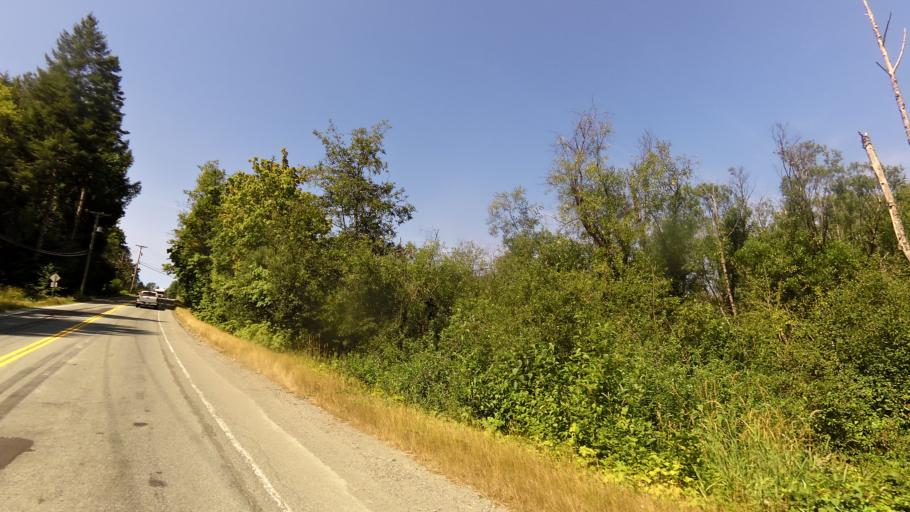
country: CA
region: British Columbia
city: Port Alberni
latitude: 49.2691
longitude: -124.8571
